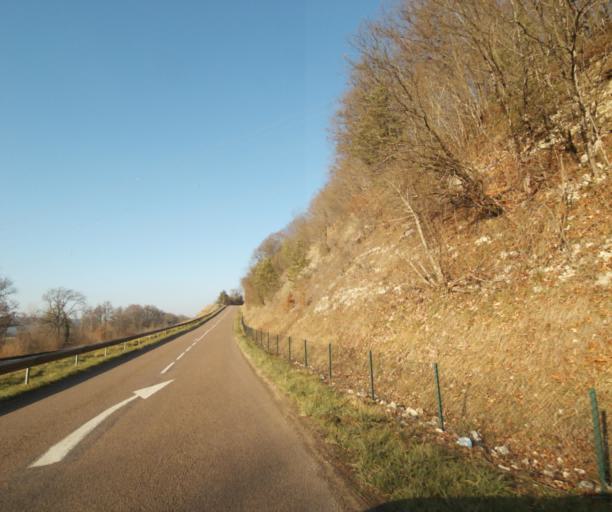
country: FR
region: Champagne-Ardenne
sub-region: Departement de la Haute-Marne
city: Chevillon
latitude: 48.5133
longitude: 5.1198
